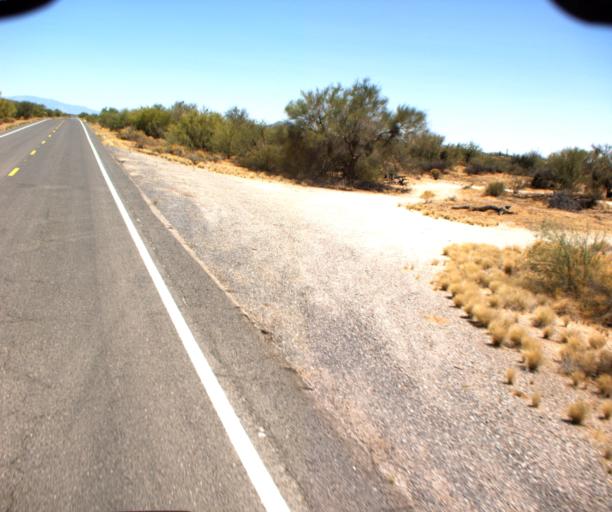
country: US
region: Arizona
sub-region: Pinal County
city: Florence
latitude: 32.8025
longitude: -111.1848
